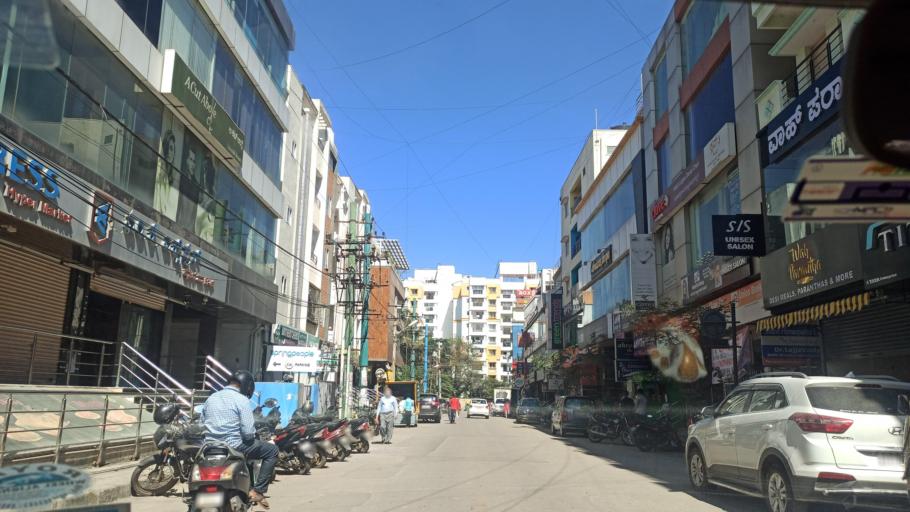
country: IN
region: Karnataka
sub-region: Bangalore Urban
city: Bangalore
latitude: 12.9262
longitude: 77.6696
